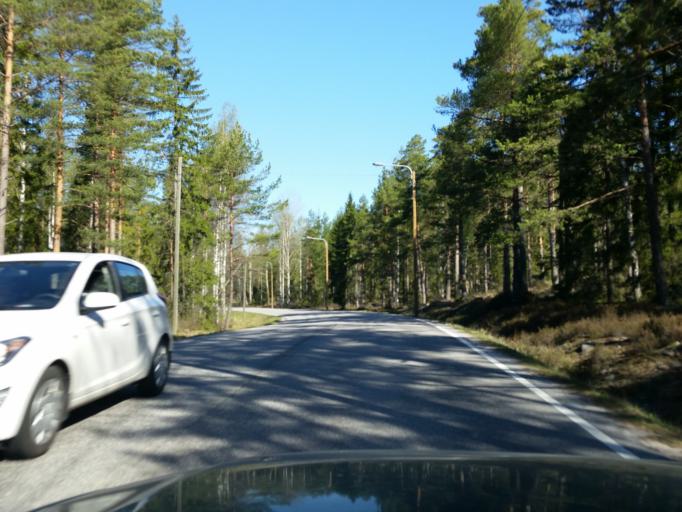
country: FI
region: Uusimaa
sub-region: Helsinki
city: Kirkkonummi
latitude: 60.1158
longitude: 24.5514
